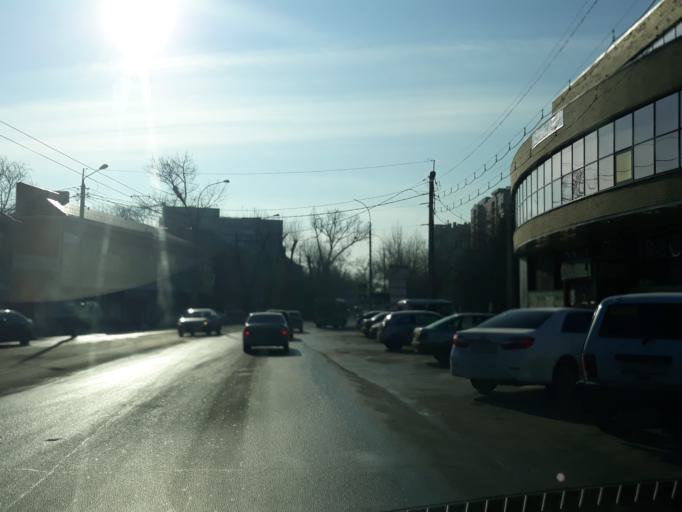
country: RU
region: Rostov
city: Taganrog
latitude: 47.2349
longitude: 38.9009
